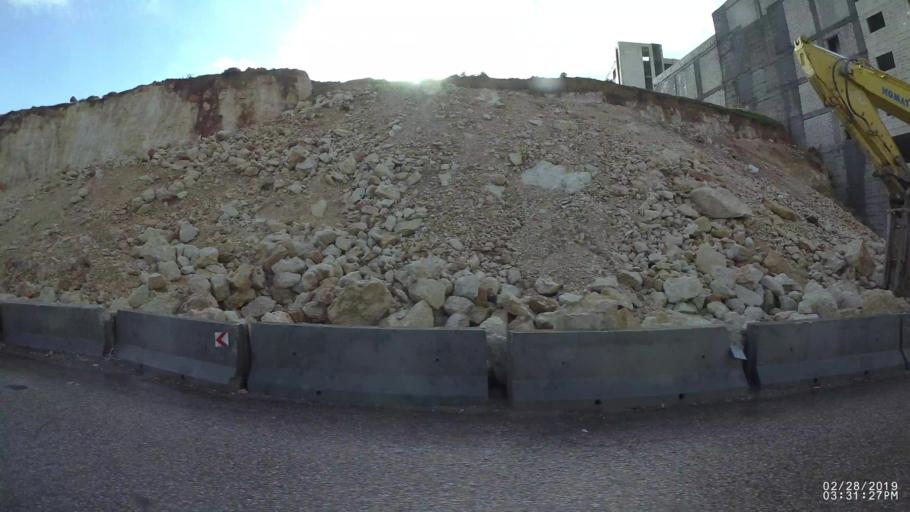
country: JO
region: Amman
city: Al Jubayhah
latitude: 32.0108
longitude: 35.8708
